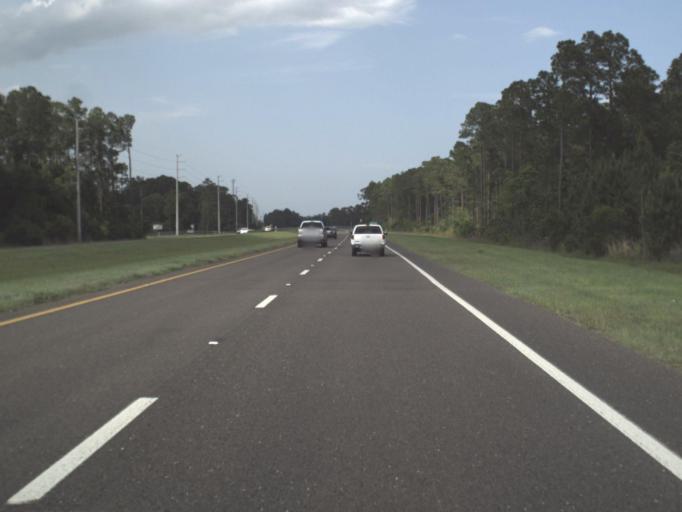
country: US
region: Florida
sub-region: Saint Johns County
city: Saint Augustine Shores
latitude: 29.7651
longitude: -81.4587
